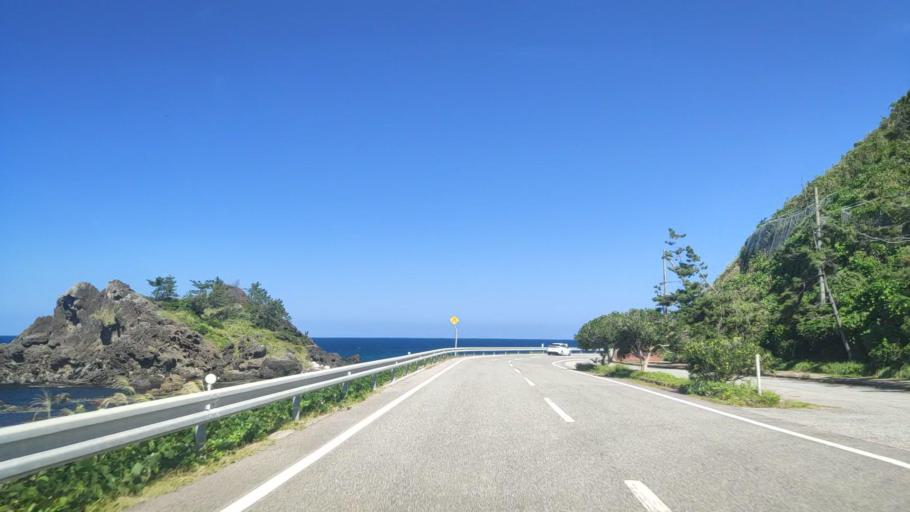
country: JP
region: Ishikawa
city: Nanao
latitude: 37.5069
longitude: 137.2001
